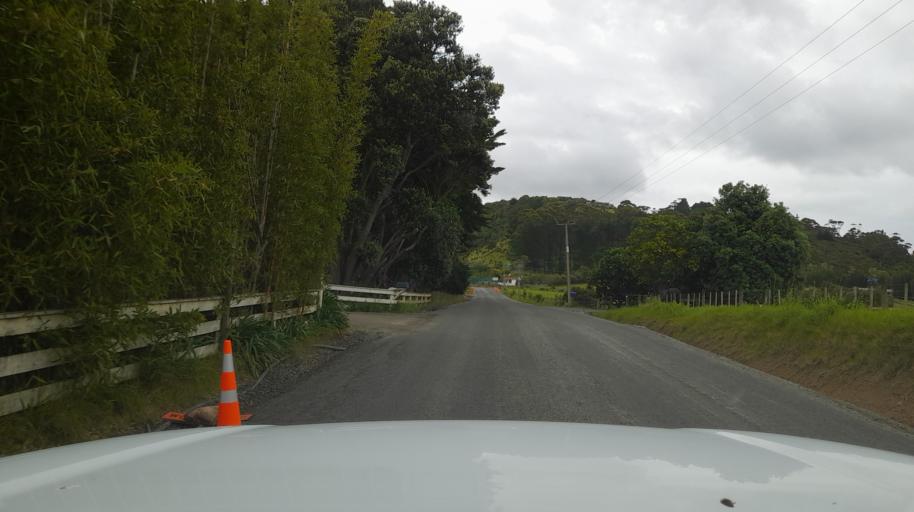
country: NZ
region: Northland
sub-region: Far North District
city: Ahipara
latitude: -35.1679
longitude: 173.1906
